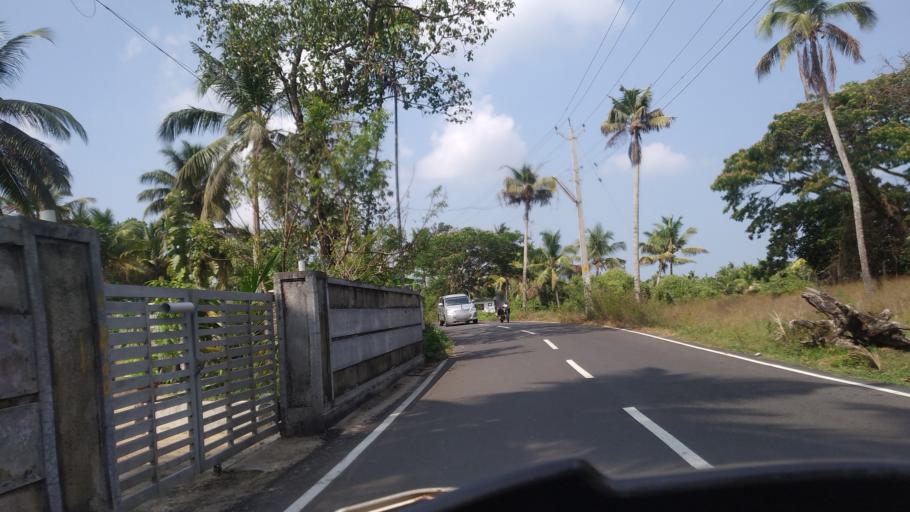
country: IN
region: Kerala
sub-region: Ernakulam
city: Elur
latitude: 10.1149
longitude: 76.2365
